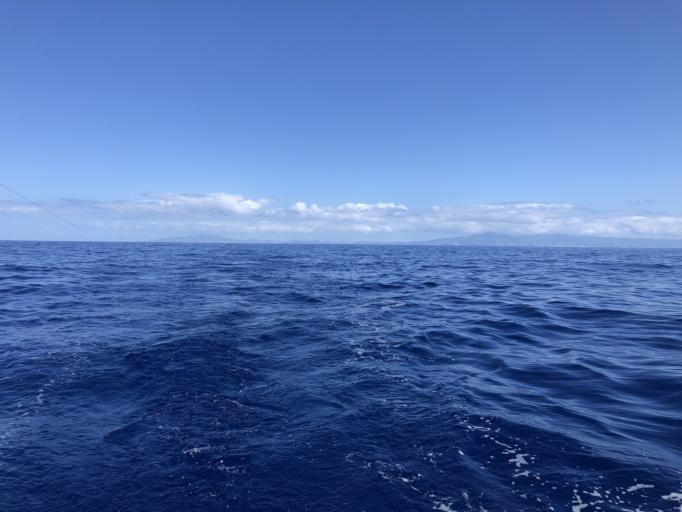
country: PT
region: Azores
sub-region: Vila Franca do Campo
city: Vila Franca do Campo
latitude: 37.4372
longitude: -25.5077
